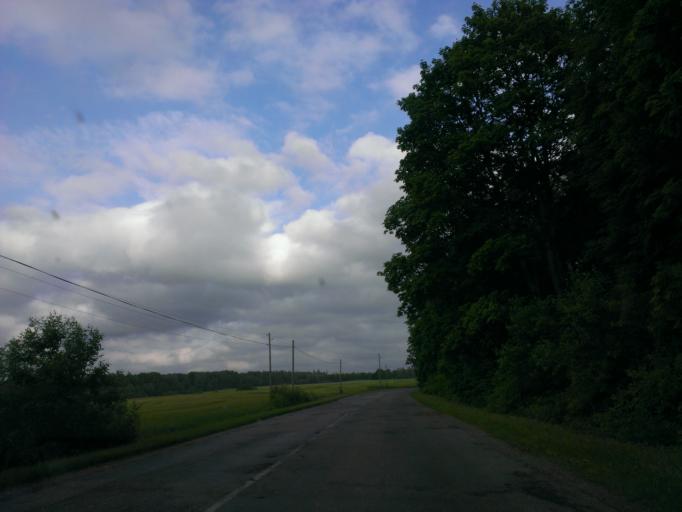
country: LV
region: Aizpute
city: Aizpute
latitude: 56.7269
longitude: 21.7436
